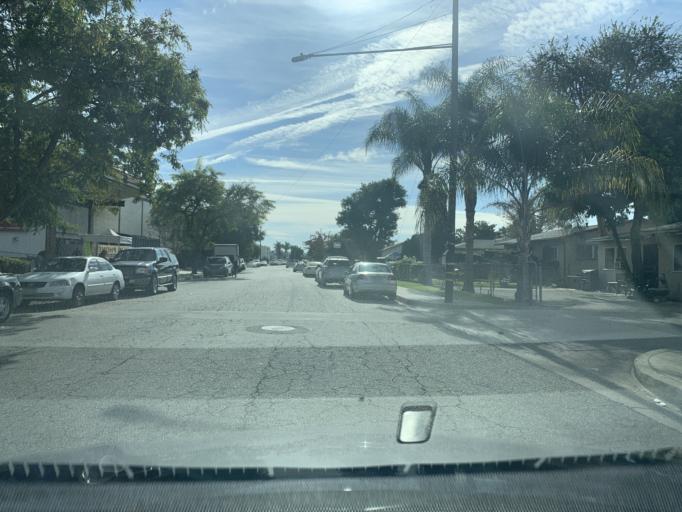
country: US
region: California
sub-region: Los Angeles County
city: South El Monte
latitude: 34.0623
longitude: -118.0530
